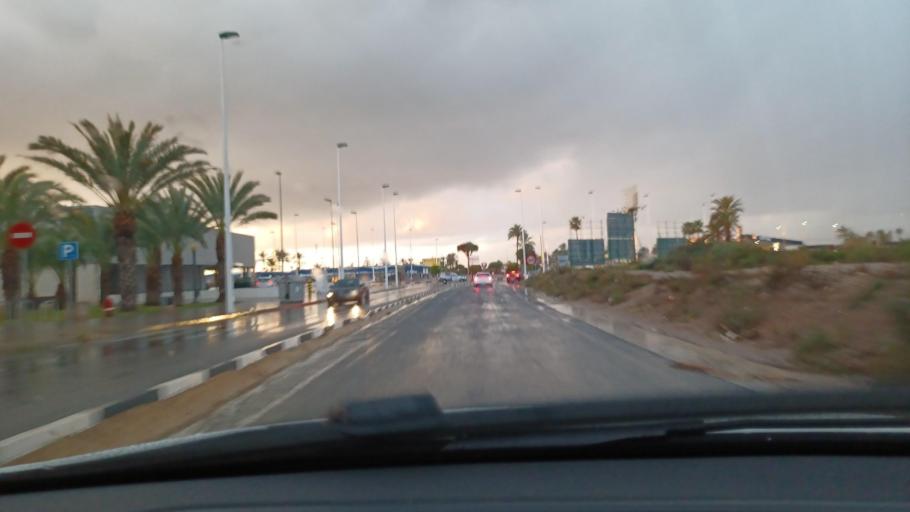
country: ES
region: Valencia
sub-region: Provincia de Alicante
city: Elche
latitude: 38.2525
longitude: -0.6972
